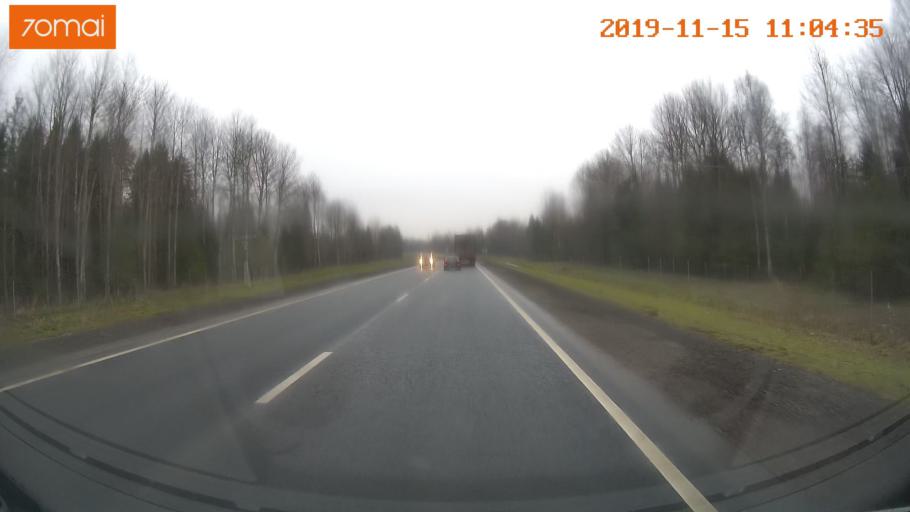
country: RU
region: Vologda
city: Chebsara
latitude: 59.1199
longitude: 38.9852
